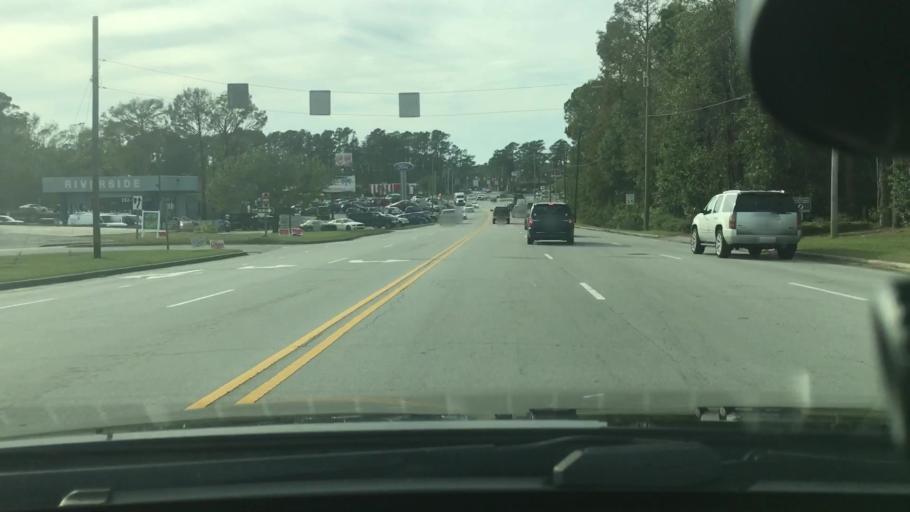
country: US
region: North Carolina
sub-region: Craven County
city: Havelock
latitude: 34.8826
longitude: -76.9069
